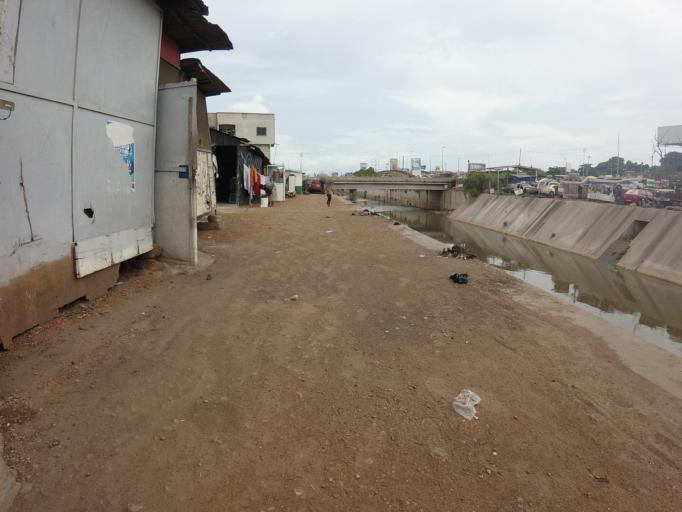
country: GH
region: Greater Accra
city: Accra
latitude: 5.5914
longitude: -0.2177
